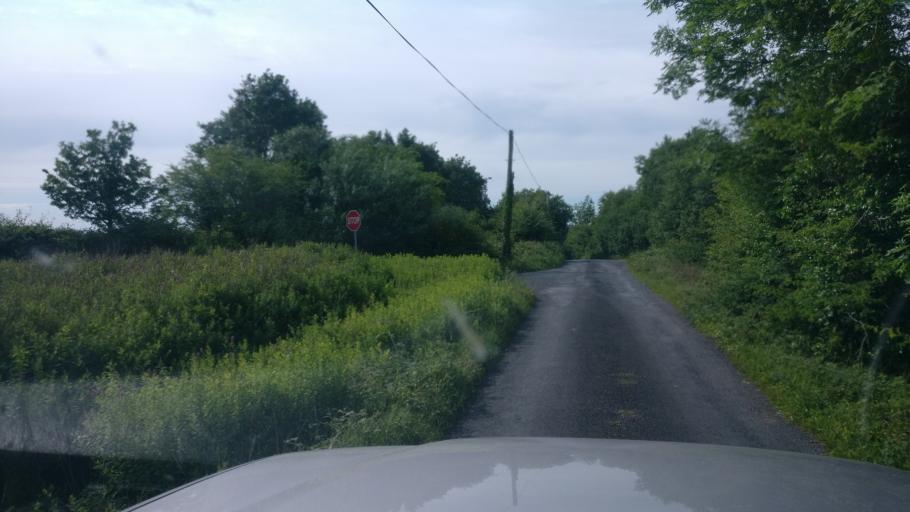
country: IE
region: Connaught
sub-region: County Galway
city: Gort
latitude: 53.0983
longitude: -8.6980
